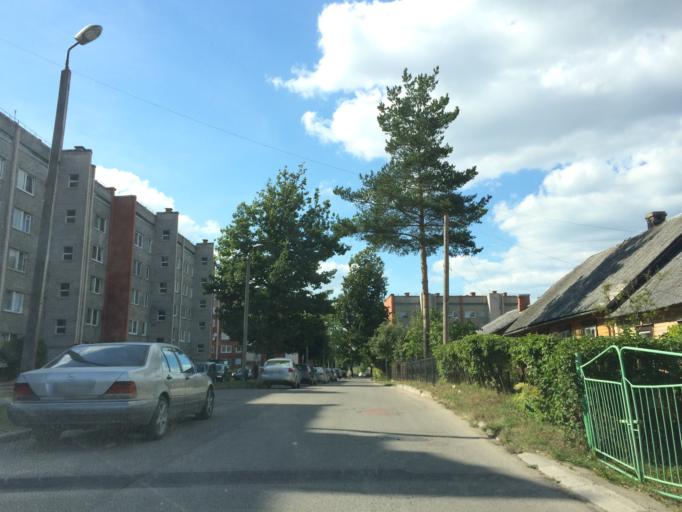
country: LV
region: Rezekne
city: Rezekne
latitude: 56.5169
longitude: 27.3436
